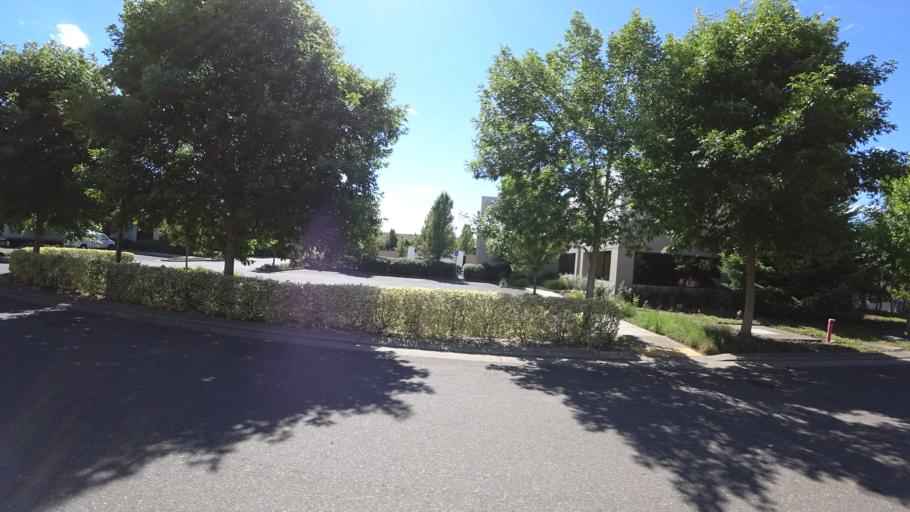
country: US
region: Oregon
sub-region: Multnomah County
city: Fairview
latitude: 45.5537
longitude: -122.4968
